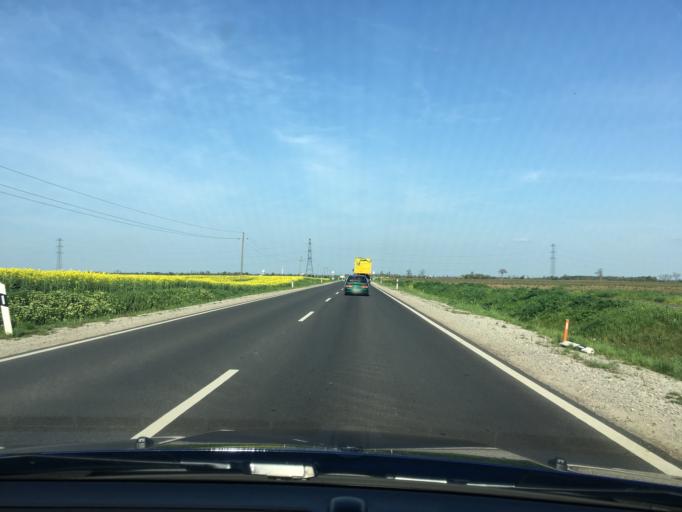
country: HU
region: Bekes
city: Ujkigyos
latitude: 46.6671
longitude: 20.9745
